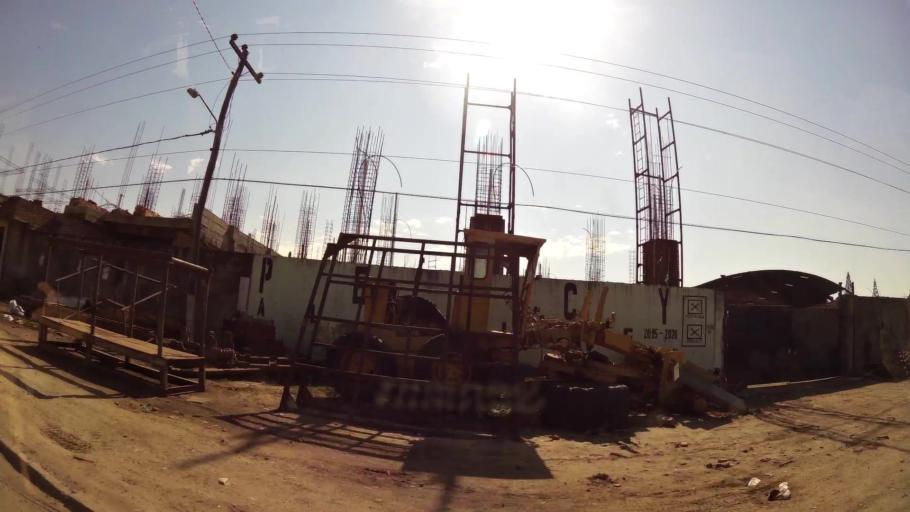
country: BO
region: Santa Cruz
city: Santa Cruz de la Sierra
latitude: -17.7613
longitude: -63.1103
